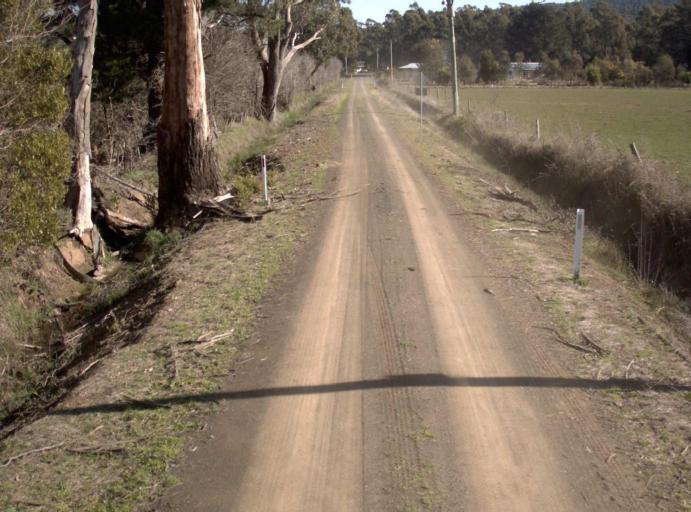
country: AU
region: Tasmania
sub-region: Launceston
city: Mayfield
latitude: -41.2540
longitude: 147.1558
